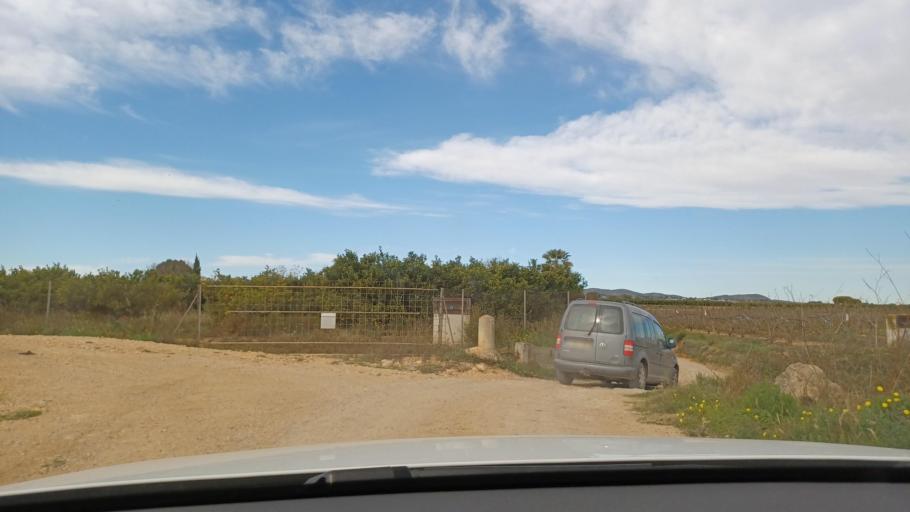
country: ES
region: Valencia
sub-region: Provincia de Valencia
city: Benifaio
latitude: 39.2925
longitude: -0.4448
